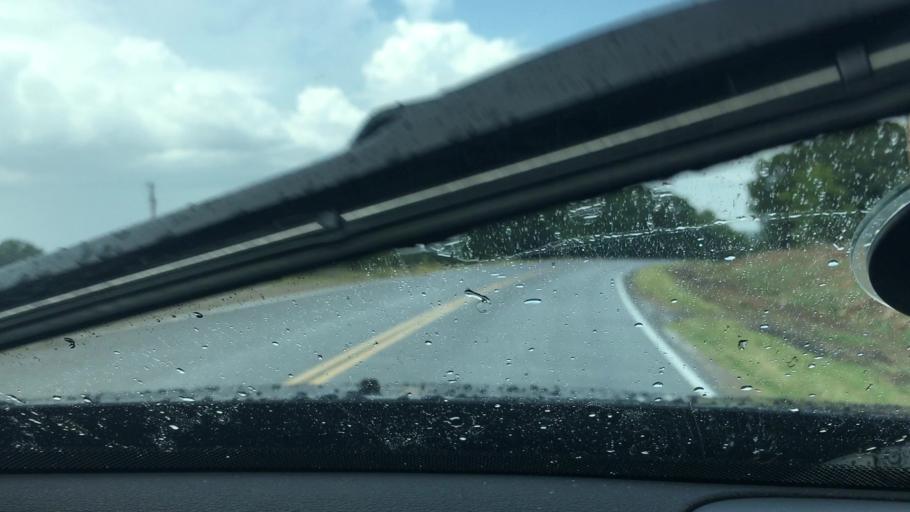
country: US
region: Oklahoma
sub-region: Johnston County
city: Tishomingo
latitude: 34.1870
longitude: -96.7239
